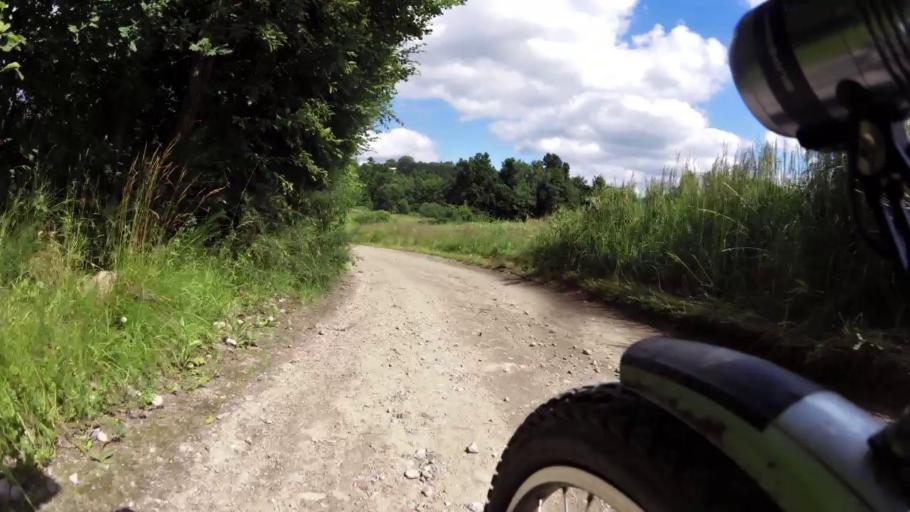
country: PL
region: West Pomeranian Voivodeship
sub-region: Powiat swidwinski
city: Rabino
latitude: 53.8608
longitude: 15.9435
